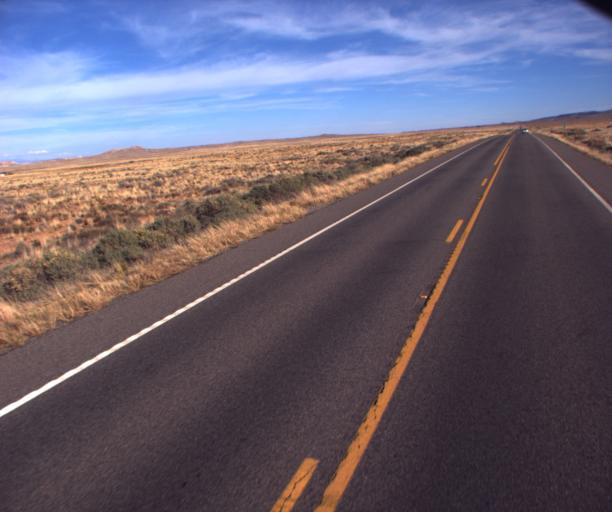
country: US
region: Arizona
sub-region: Apache County
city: Lukachukai
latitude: 36.9503
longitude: -109.2823
